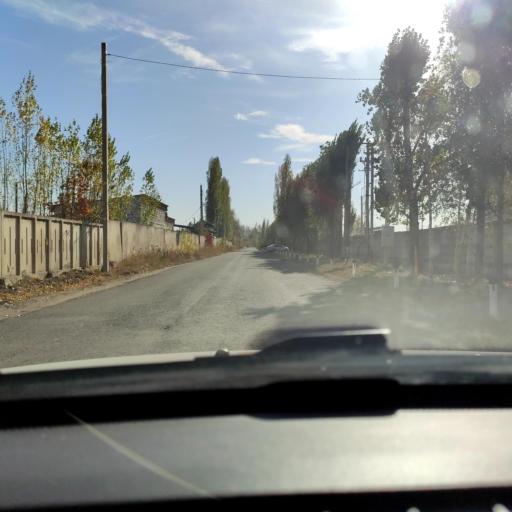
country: RU
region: Voronezj
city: Podgornoye
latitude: 51.8064
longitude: 39.2001
